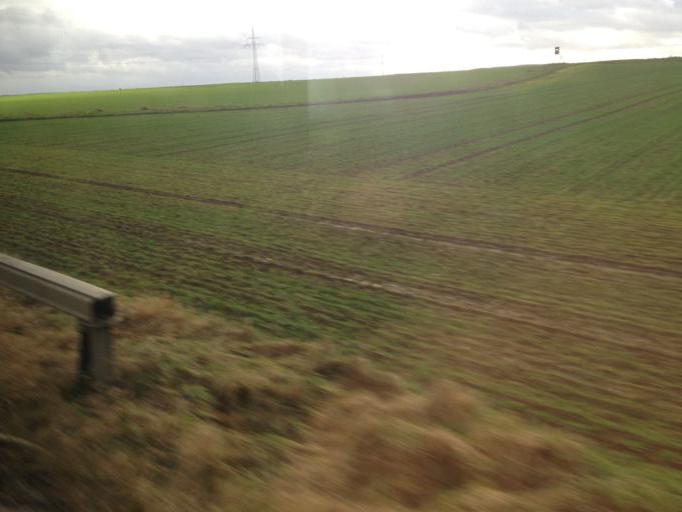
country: DE
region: Hesse
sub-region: Regierungsbezirk Giessen
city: Lich
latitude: 50.5074
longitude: 8.8432
